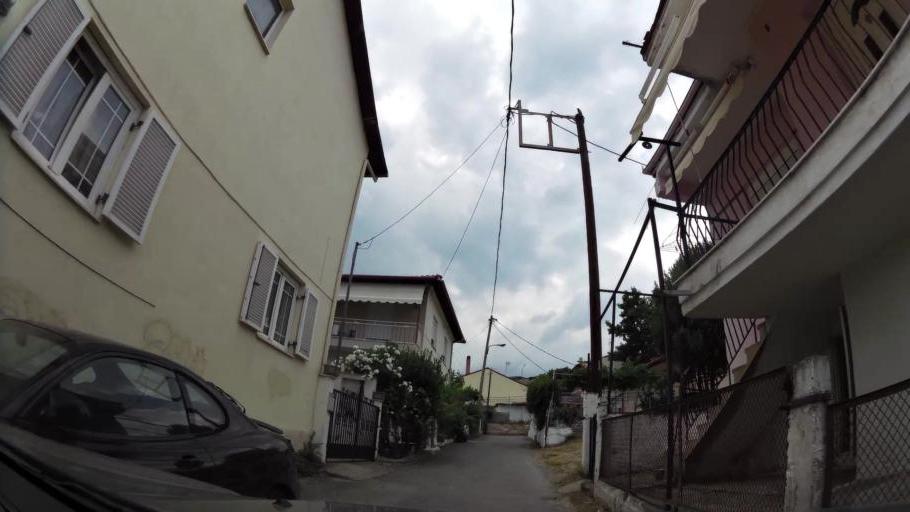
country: GR
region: Central Macedonia
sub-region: Nomos Imathias
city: Veroia
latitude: 40.5200
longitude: 22.2080
